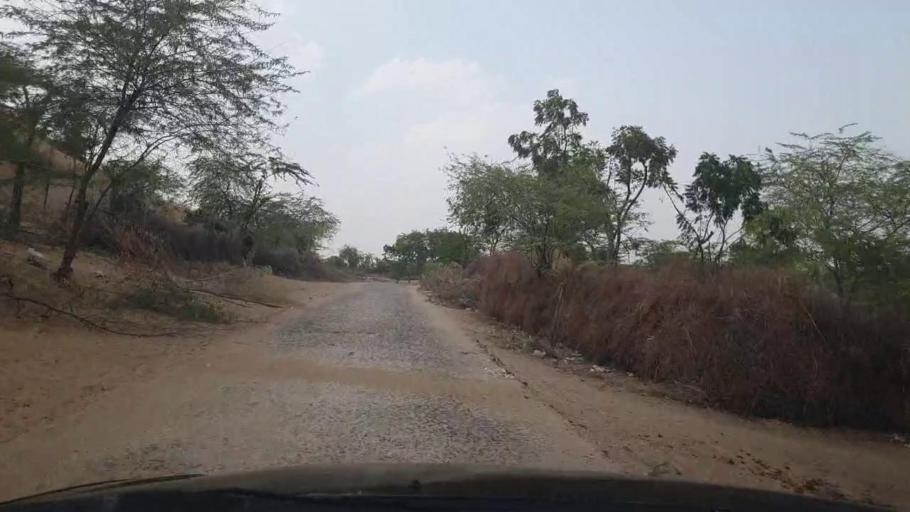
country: PK
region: Sindh
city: Islamkot
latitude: 24.9545
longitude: 70.6360
